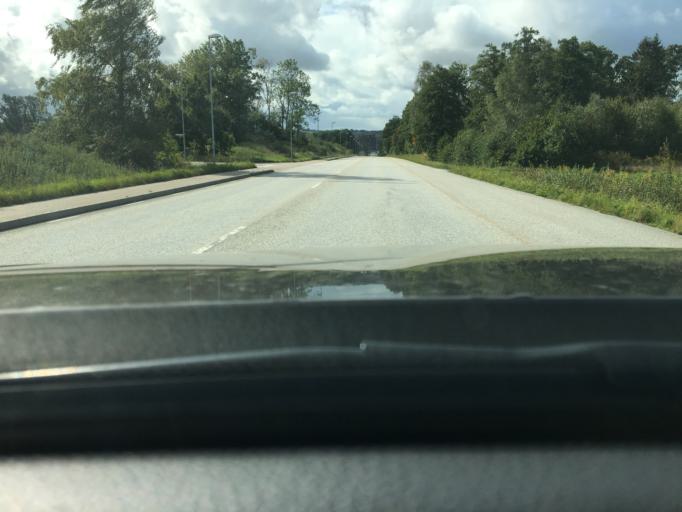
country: SE
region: Skane
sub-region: Horby Kommun
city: Hoerby
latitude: 55.8604
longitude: 13.6817
